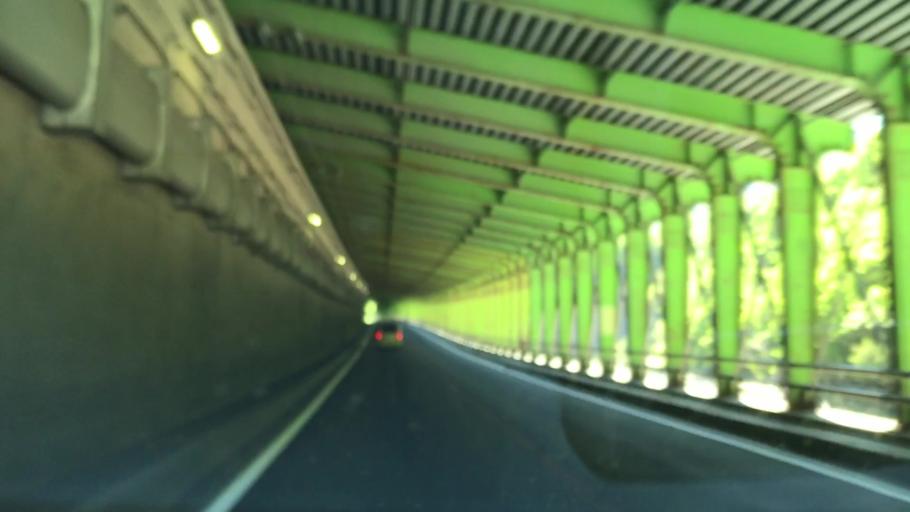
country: JP
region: Hokkaido
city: Shimo-furano
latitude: 42.9374
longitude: 142.5987
